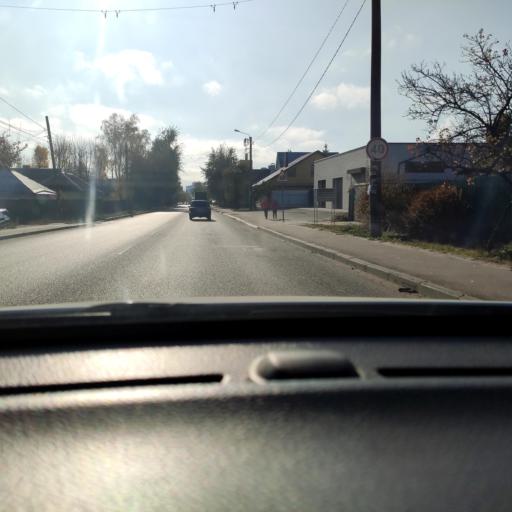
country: RU
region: Voronezj
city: Voronezh
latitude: 51.6993
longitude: 39.1639
